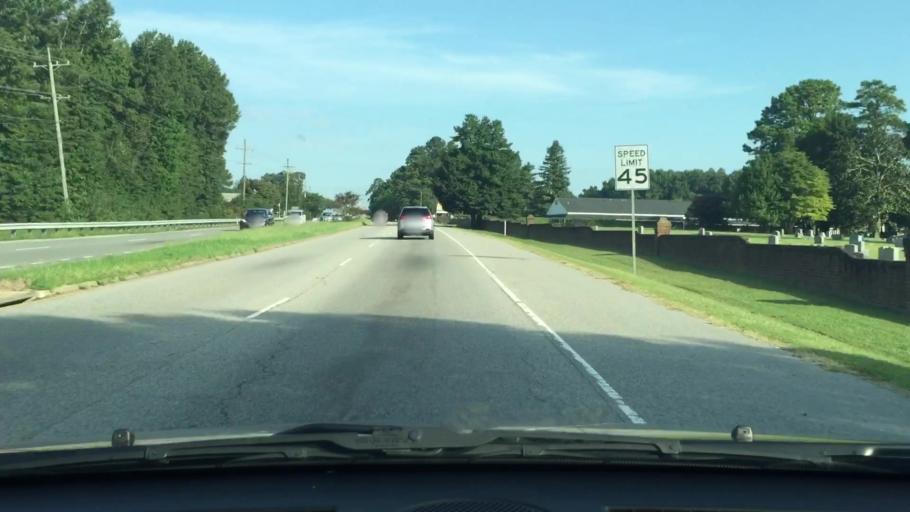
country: US
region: Virginia
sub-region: Isle of Wight County
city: Carrollton
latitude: 36.9407
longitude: -76.5882
